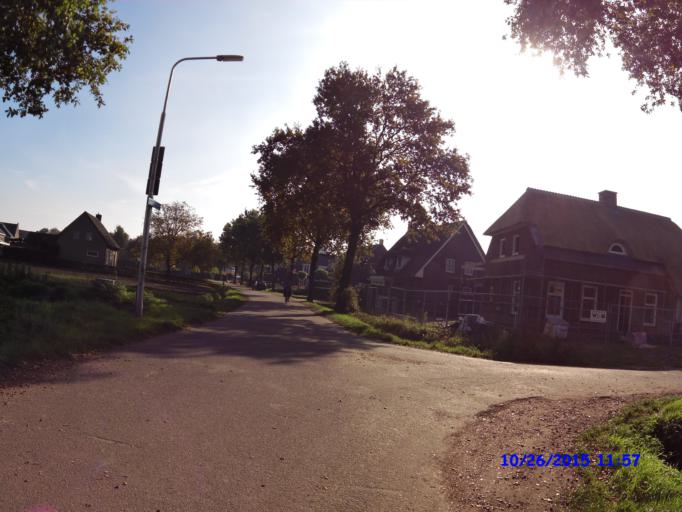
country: NL
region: North Brabant
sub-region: Gemeente Geldrop-Mierlo
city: Mierlo
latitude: 51.4410
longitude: 5.6018
